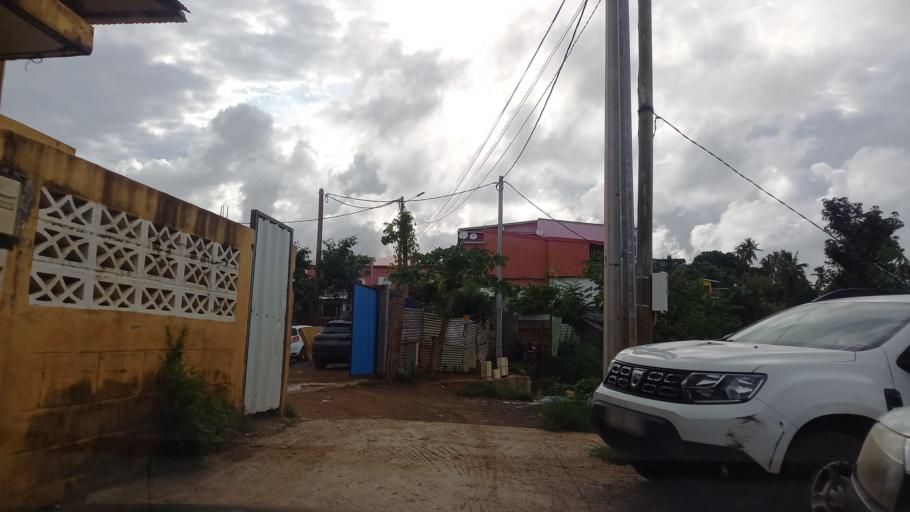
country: YT
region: Sada
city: Sada
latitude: -12.8530
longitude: 45.0962
